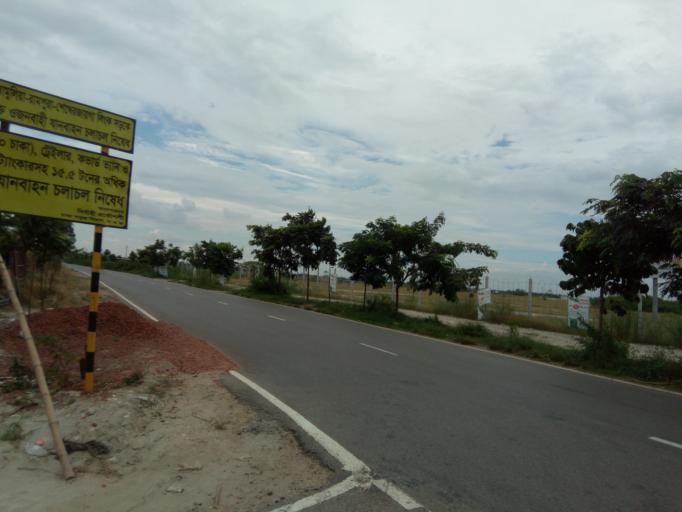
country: BD
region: Dhaka
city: Paltan
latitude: 23.7465
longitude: 90.4721
